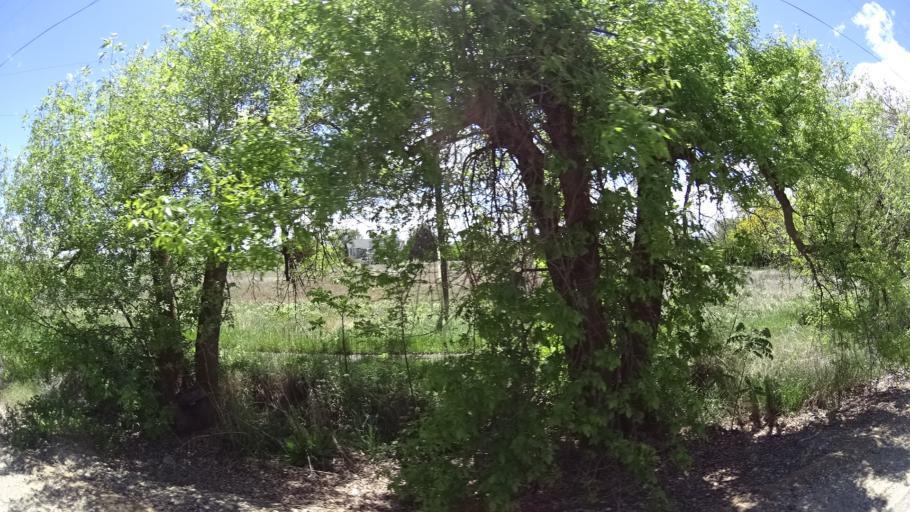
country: US
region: Idaho
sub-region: Ada County
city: Meridian
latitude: 43.5903
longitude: -116.4692
